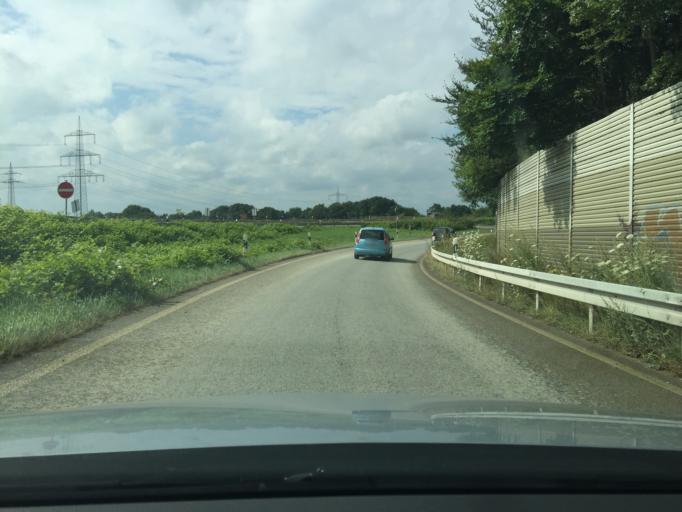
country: DE
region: North Rhine-Westphalia
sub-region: Regierungsbezirk Dusseldorf
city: Velbert
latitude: 51.3305
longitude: 7.0144
